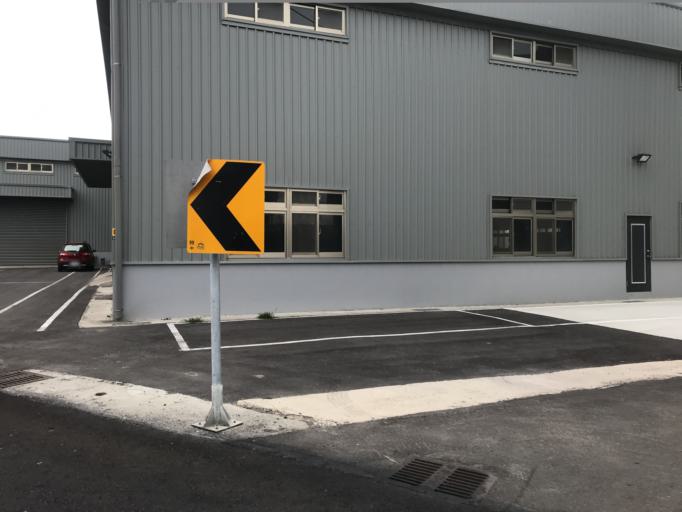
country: TW
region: Taiwan
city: Fengyuan
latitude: 24.3696
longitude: 120.6015
